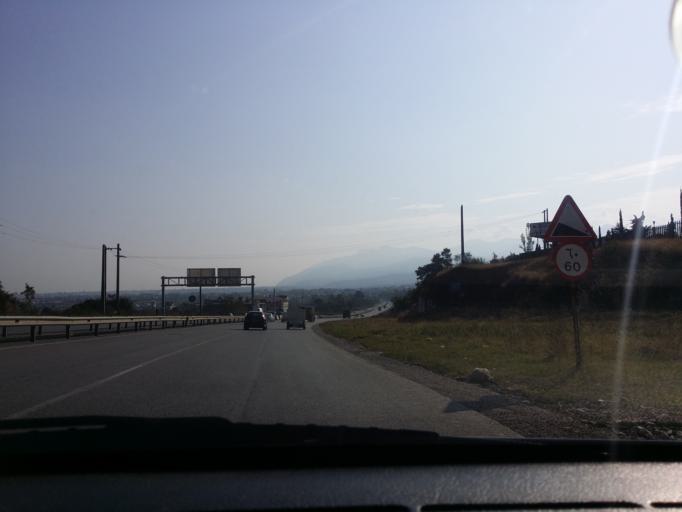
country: IR
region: Mazandaran
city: Chalus
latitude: 36.6435
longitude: 51.4262
